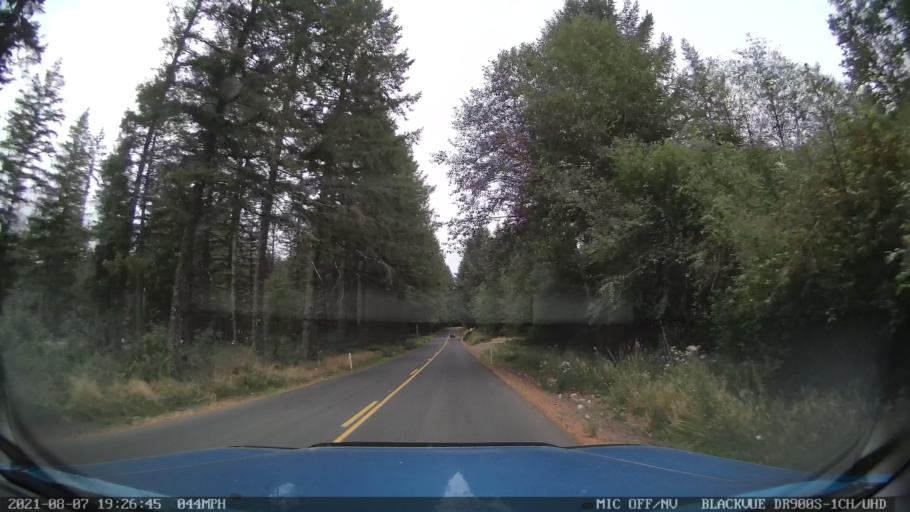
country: US
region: Oregon
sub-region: Linn County
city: Lyons
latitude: 44.8745
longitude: -122.6516
